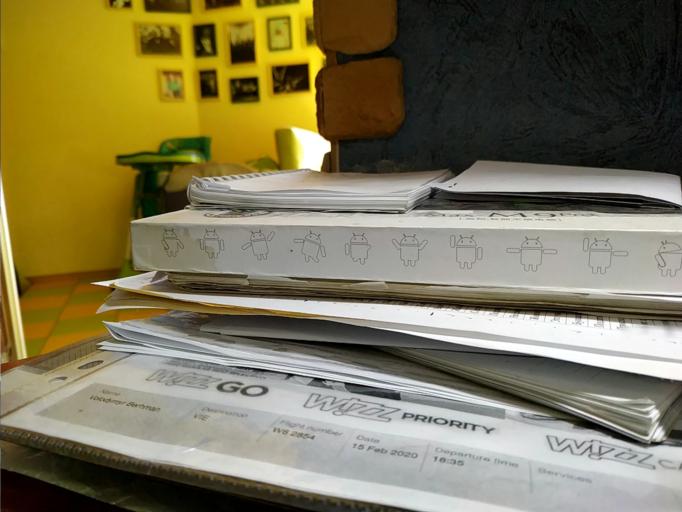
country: RU
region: Pskov
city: Plyussa
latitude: 58.6541
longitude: 29.3395
